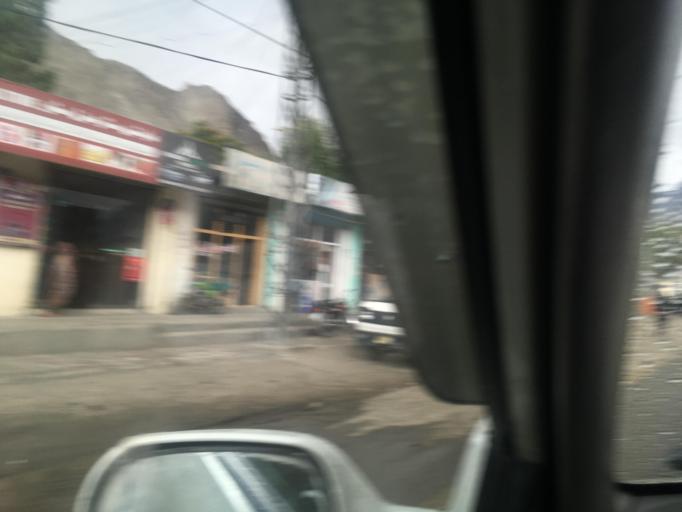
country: PK
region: Gilgit-Baltistan
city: Skardu
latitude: 35.3025
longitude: 75.6248
